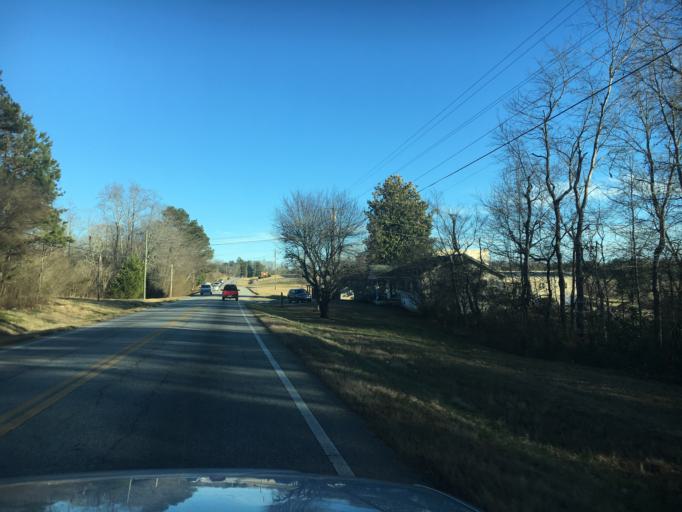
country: US
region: Georgia
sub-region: Habersham County
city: Demorest
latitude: 34.5493
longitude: -83.5603
